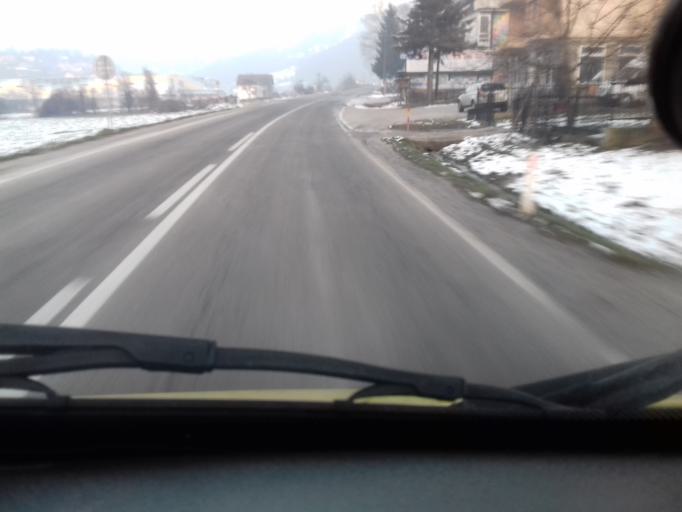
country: BA
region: Federation of Bosnia and Herzegovina
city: Vogosca
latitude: 43.8834
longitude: 18.3204
